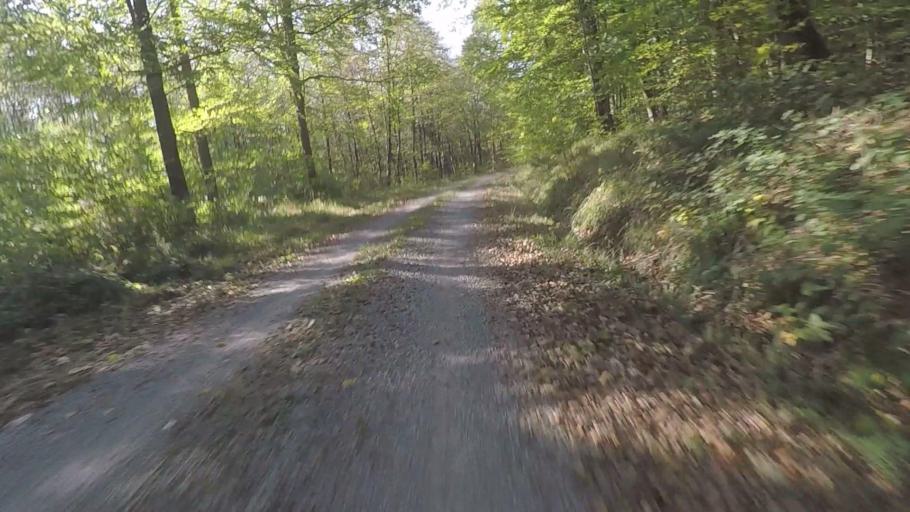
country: DE
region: Baden-Wuerttemberg
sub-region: Regierungsbezirk Stuttgart
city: Spiegelberg
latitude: 49.0362
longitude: 9.4743
